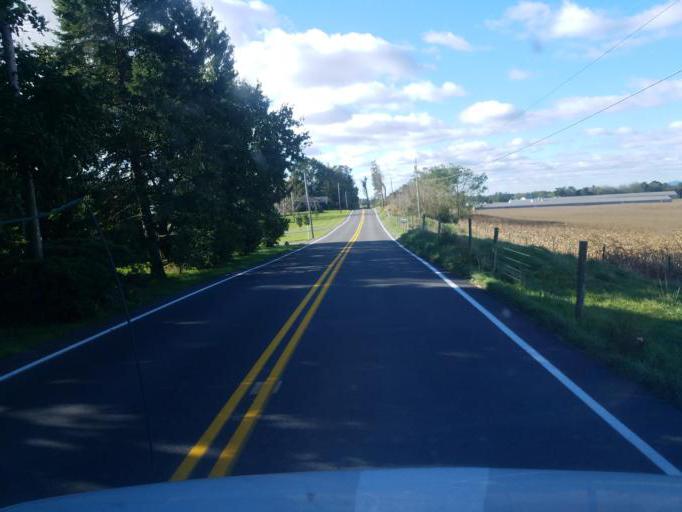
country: US
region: Pennsylvania
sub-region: Franklin County
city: Guilford Siding
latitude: 39.8204
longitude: -77.6408
